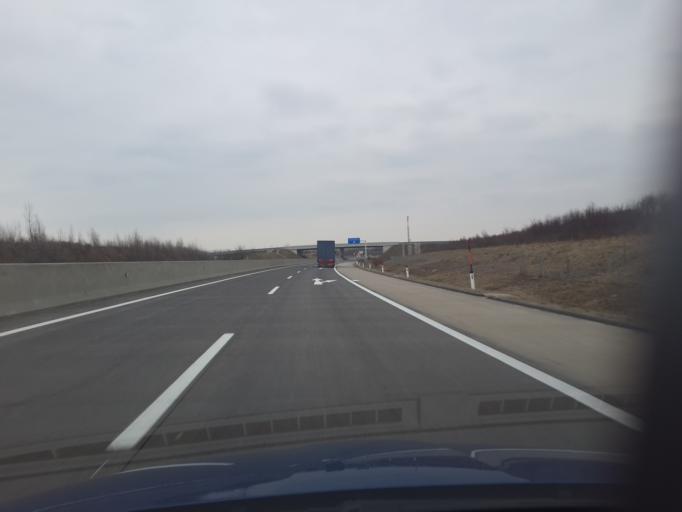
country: AT
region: Burgenland
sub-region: Politischer Bezirk Neusiedl am See
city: Gattendorf
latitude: 48.0382
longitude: 16.9878
